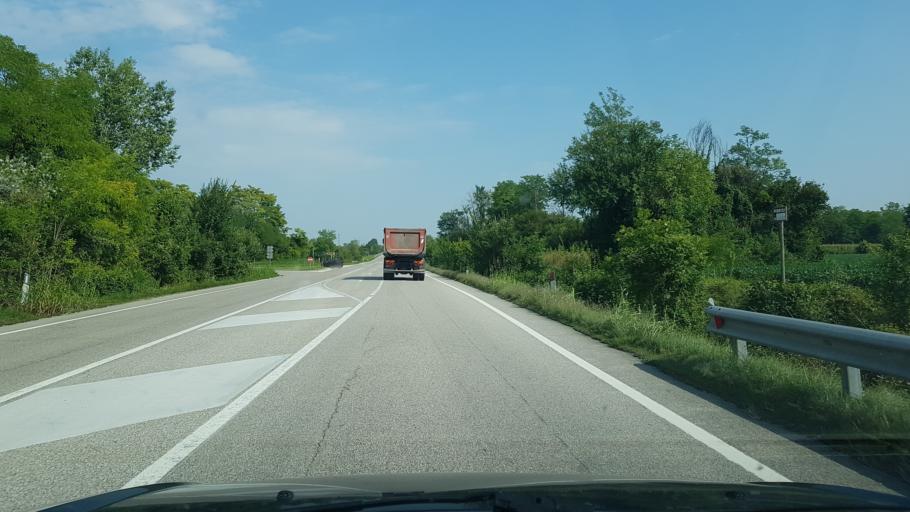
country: IT
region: Friuli Venezia Giulia
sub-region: Provincia di Pordenone
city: Spilimbergo
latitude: 46.0977
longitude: 12.8683
